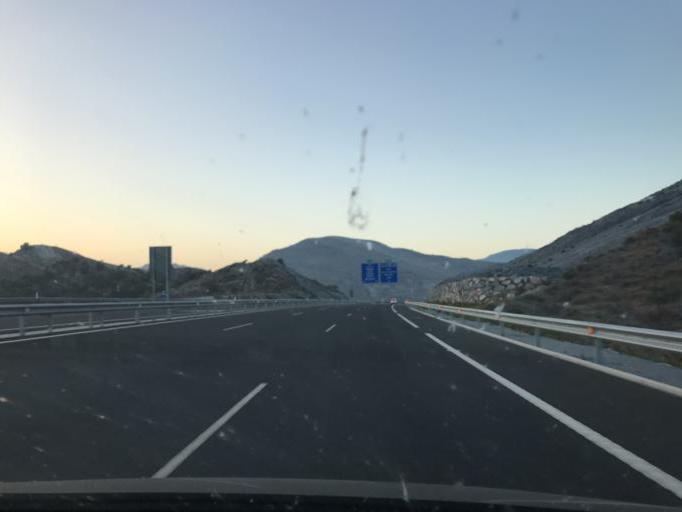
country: ES
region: Andalusia
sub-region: Provincia de Granada
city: Motril
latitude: 36.7789
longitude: -3.5015
